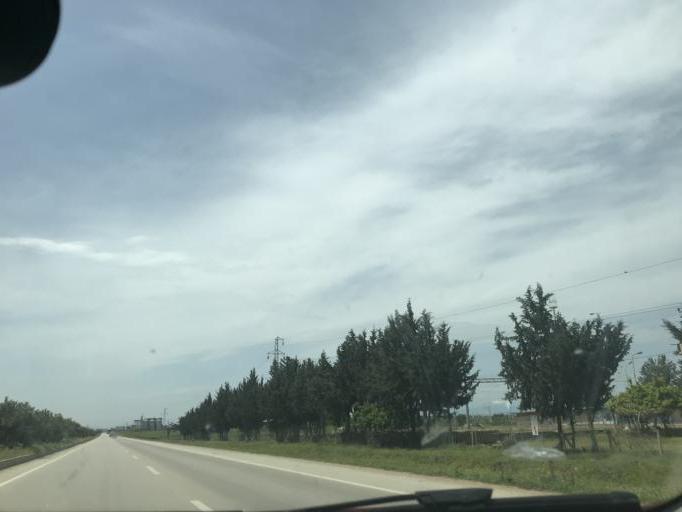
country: TR
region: Adana
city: Yuregir
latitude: 36.9758
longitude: 35.4861
